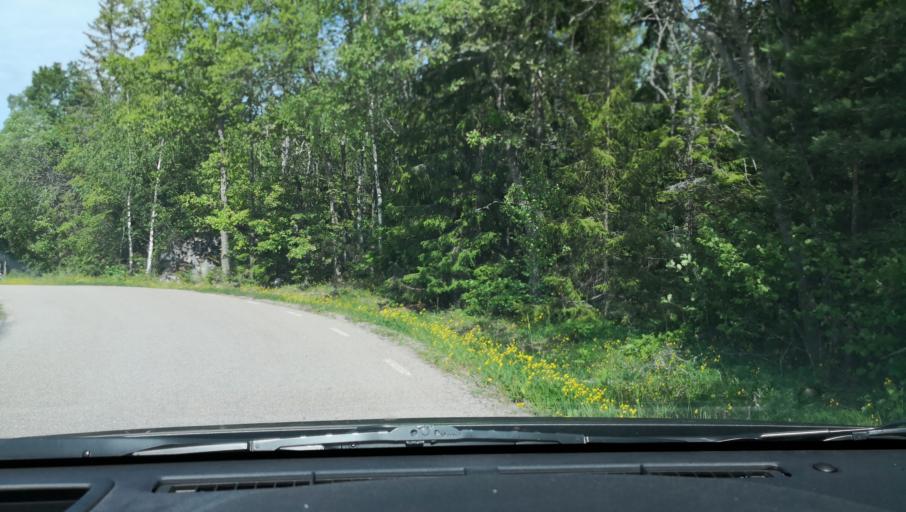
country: SE
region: Uppsala
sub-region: Uppsala Kommun
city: Alsike
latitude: 59.7029
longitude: 17.6510
